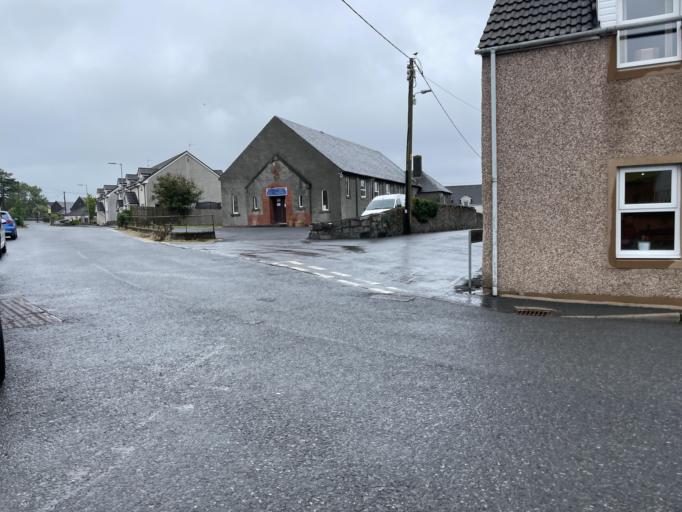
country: GB
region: Scotland
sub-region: Dumfries and Galloway
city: Newton Stewart
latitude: 54.8686
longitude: -4.4450
